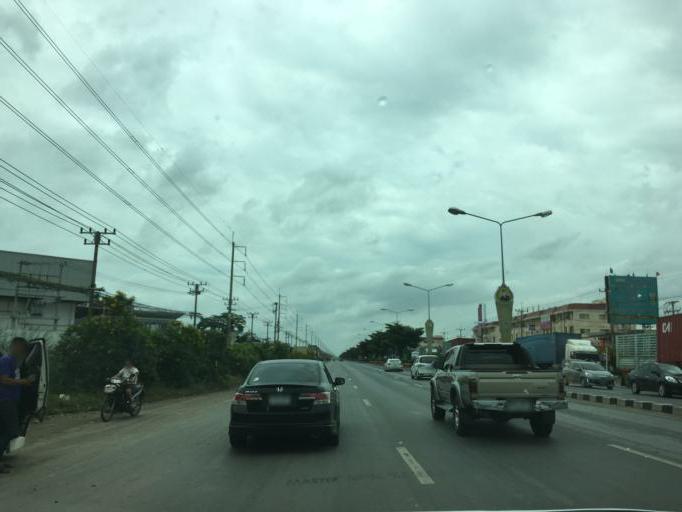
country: TH
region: Phra Nakhon Si Ayutthaya
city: Uthai
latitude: 14.2919
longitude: 100.6620
